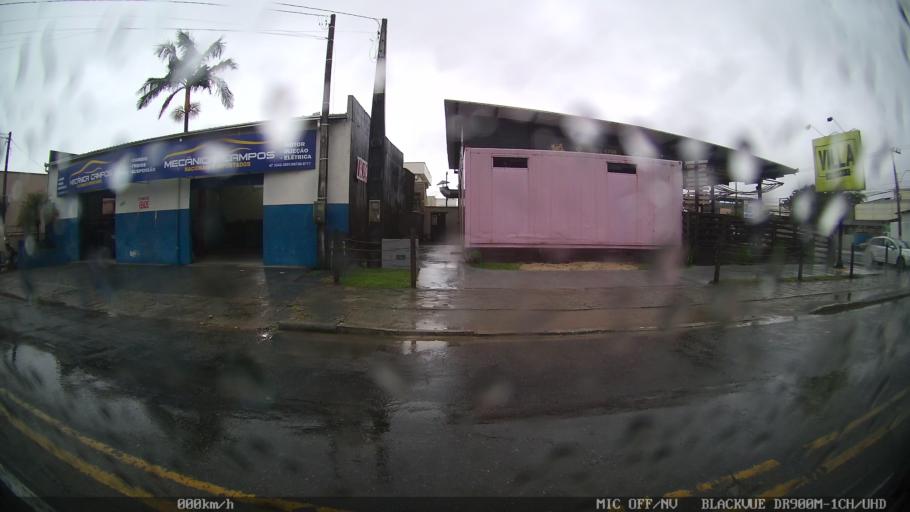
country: BR
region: Santa Catarina
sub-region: Navegantes
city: Navegantes
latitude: -26.8806
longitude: -48.6445
